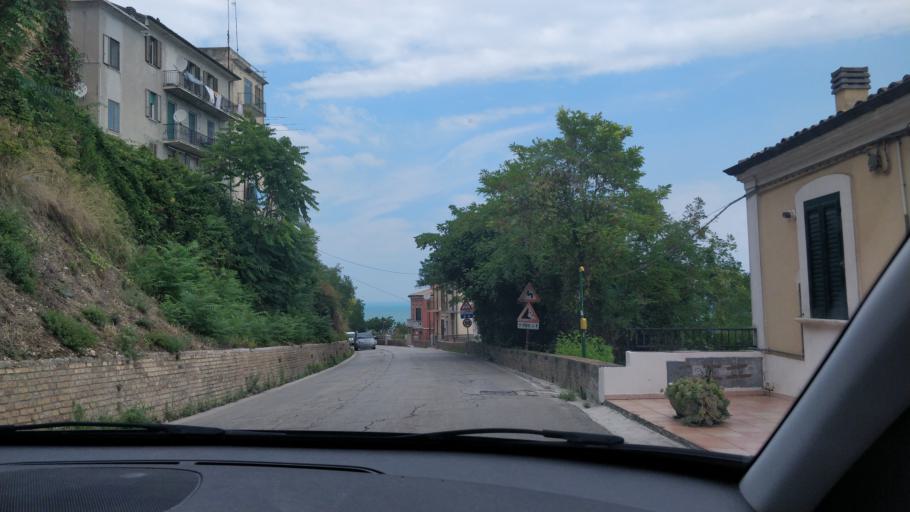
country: IT
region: Abruzzo
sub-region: Provincia di Chieti
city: Marina di San Vito
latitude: 42.3033
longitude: 14.4465
